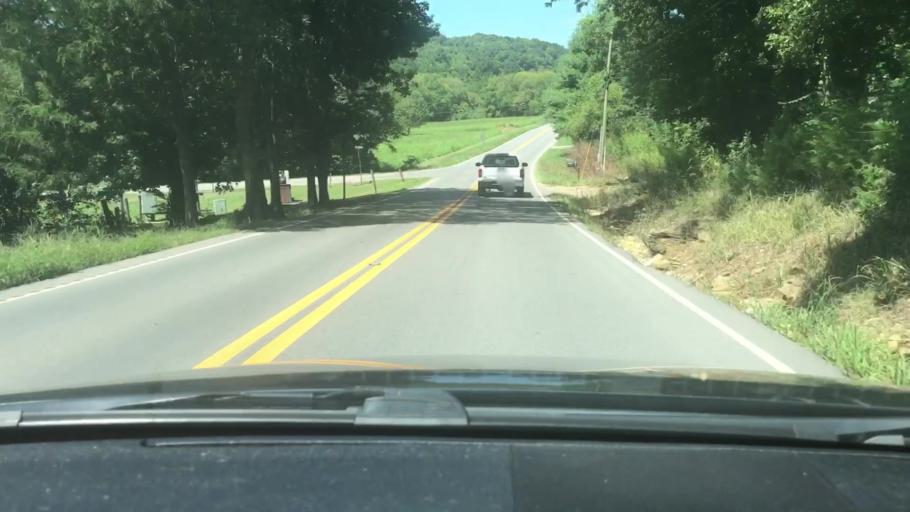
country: US
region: Tennessee
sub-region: Sumner County
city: White House
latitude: 36.4582
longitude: -86.5522
